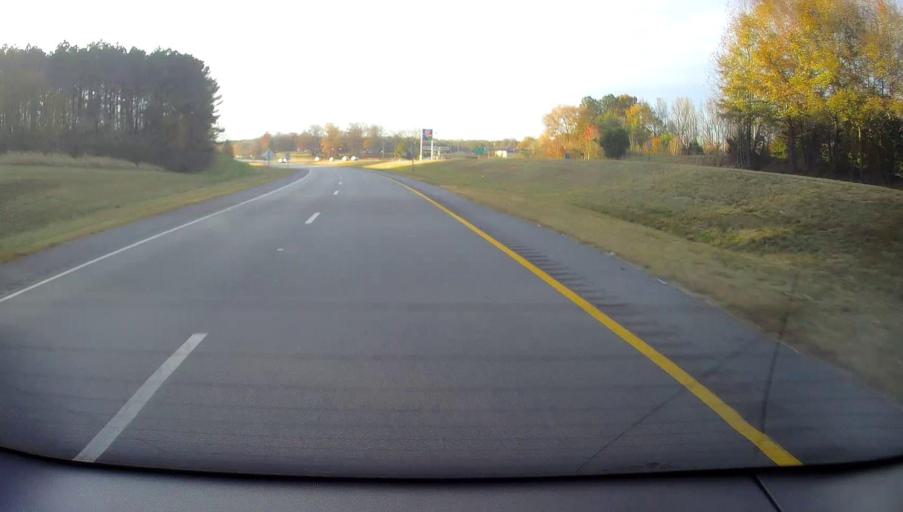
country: US
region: Alabama
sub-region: Blount County
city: Blountsville
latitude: 34.1611
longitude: -86.4723
